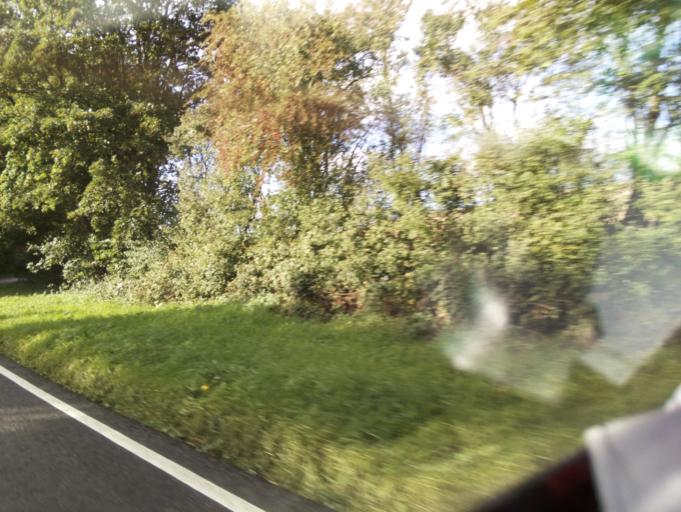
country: GB
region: England
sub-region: Hampshire
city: Four Marks
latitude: 51.1749
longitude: -1.0536
